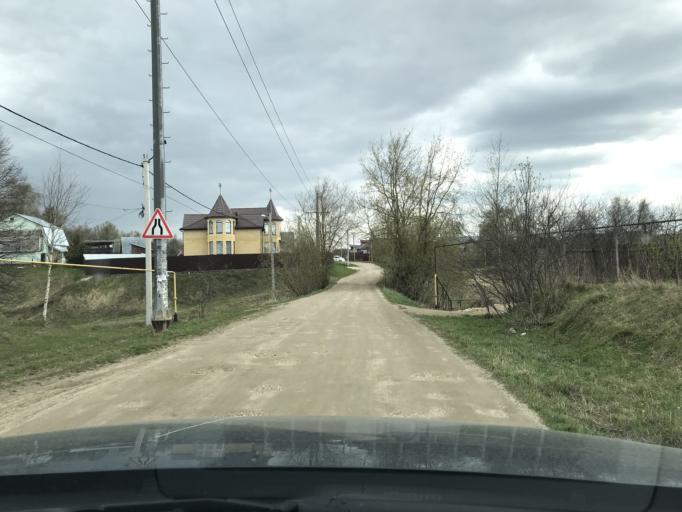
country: RU
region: Vladimir
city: Strunino
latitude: 56.3823
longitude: 38.5933
